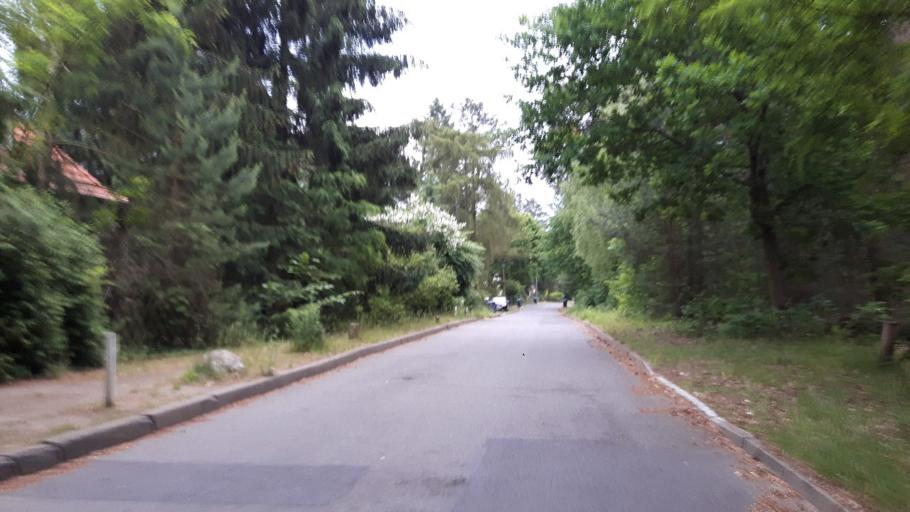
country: DE
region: Berlin
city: Wannsee
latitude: 52.4034
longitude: 13.1769
